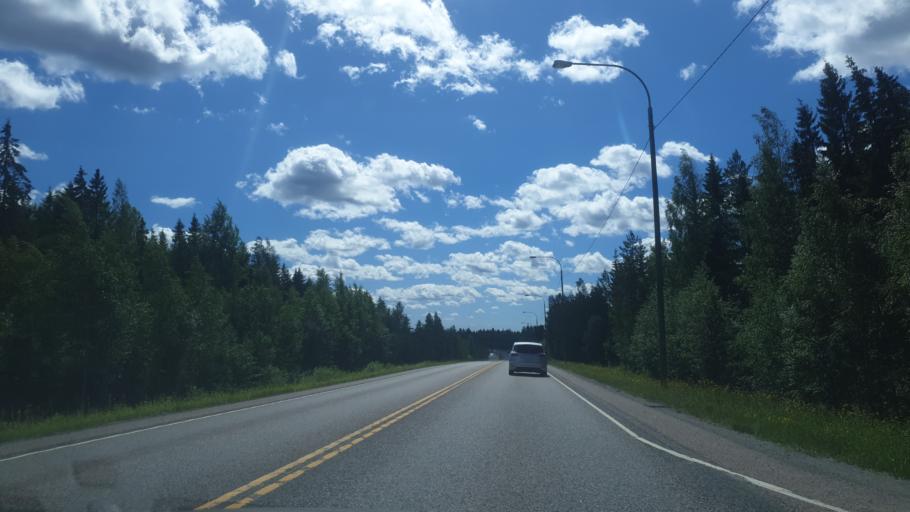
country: FI
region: Northern Savo
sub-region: Varkaus
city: Varkaus
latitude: 62.3674
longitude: 27.8098
